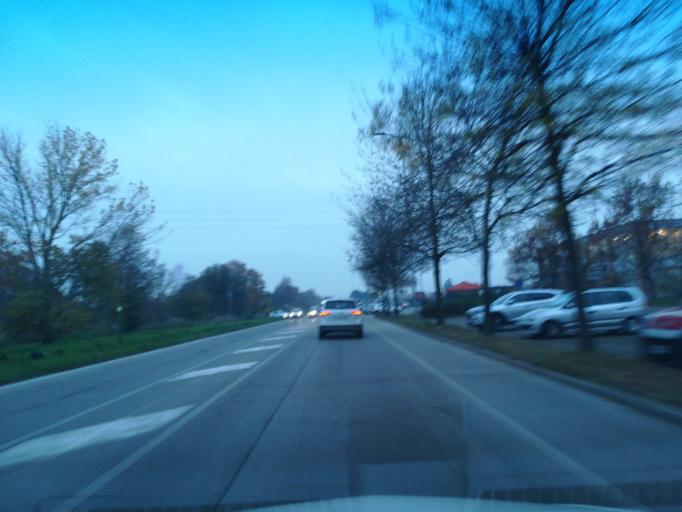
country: IT
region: Emilia-Romagna
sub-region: Provincia di Ravenna
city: Faenza
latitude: 44.3070
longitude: 11.8954
